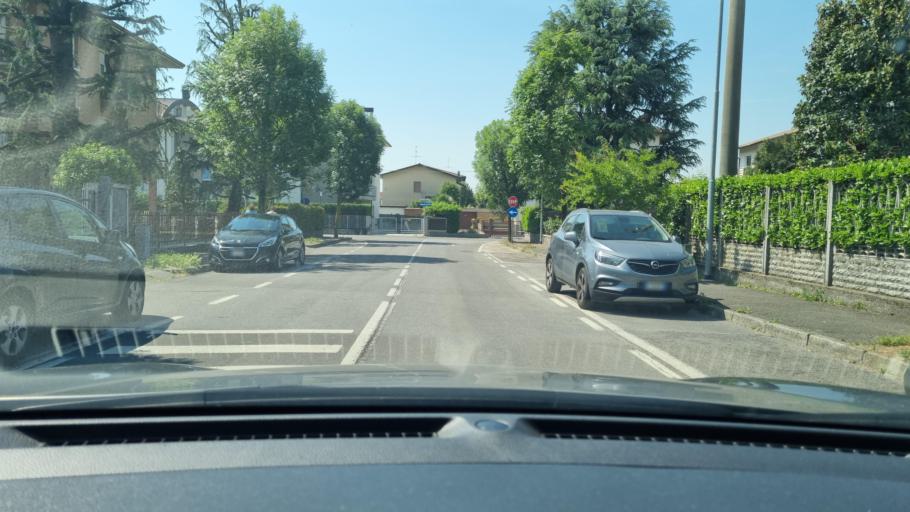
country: IT
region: Lombardy
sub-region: Provincia di Bergamo
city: Stezzano
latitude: 45.6471
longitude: 9.6581
